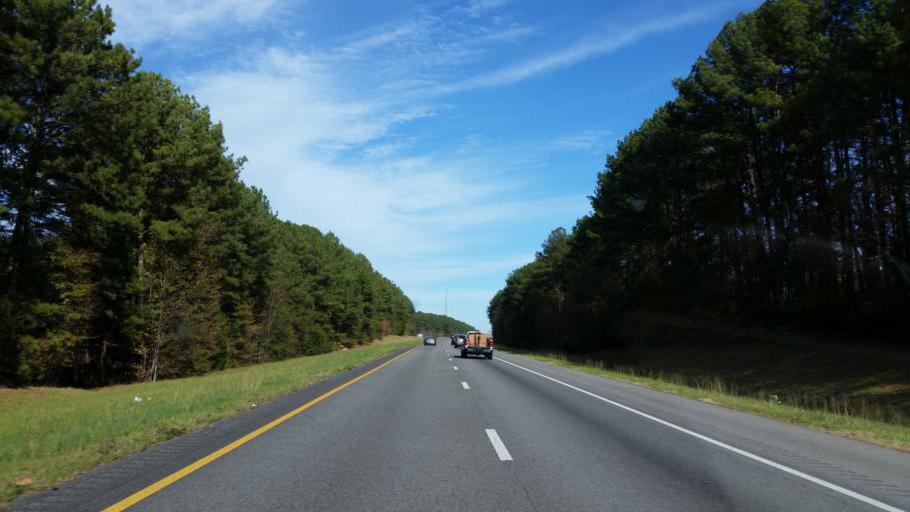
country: US
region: Alabama
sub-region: Sumter County
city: York
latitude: 32.5025
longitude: -88.3307
